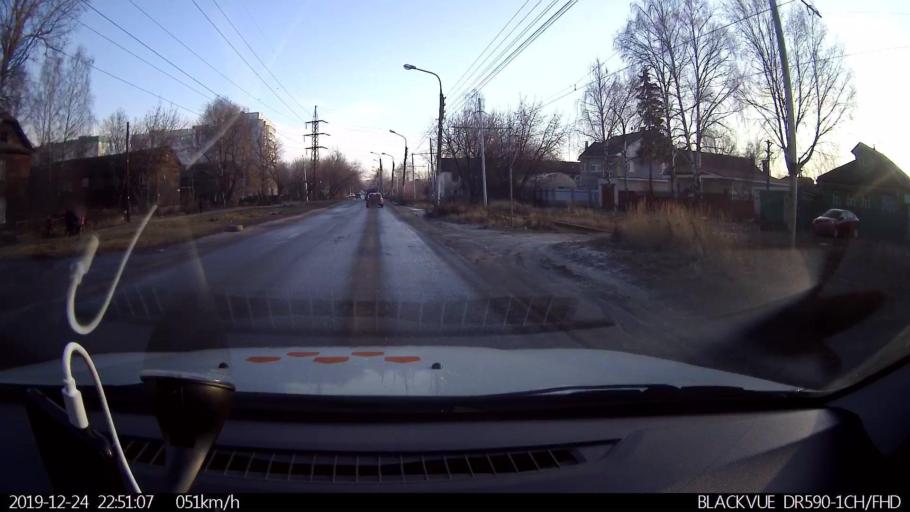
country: RU
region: Nizjnij Novgorod
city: Nizhniy Novgorod
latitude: 56.2890
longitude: 43.9067
